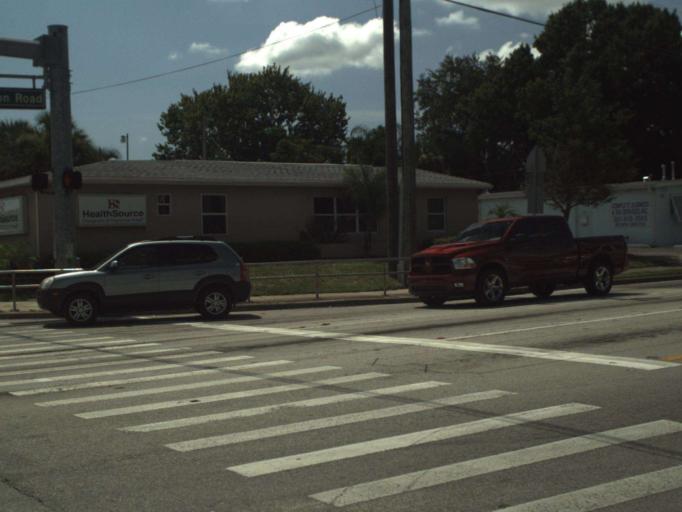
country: US
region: Florida
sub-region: Brevard County
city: West Melbourne
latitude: 28.1287
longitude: -80.6551
